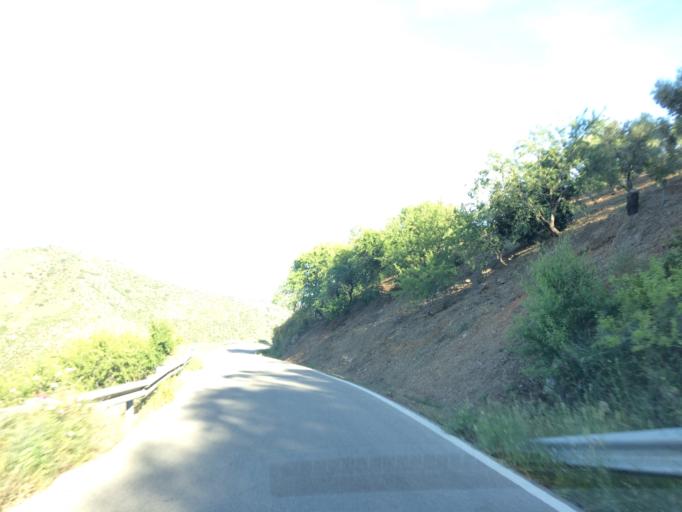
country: ES
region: Andalusia
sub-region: Provincia de Malaga
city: Totalan
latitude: 36.7796
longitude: -4.3182
